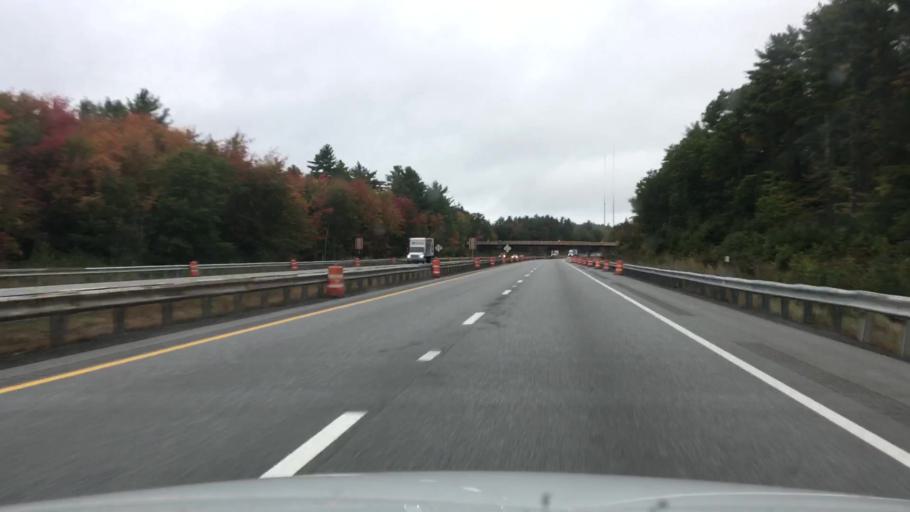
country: US
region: Maine
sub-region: Cumberland County
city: Cumberland Center
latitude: 43.8343
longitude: -70.3237
